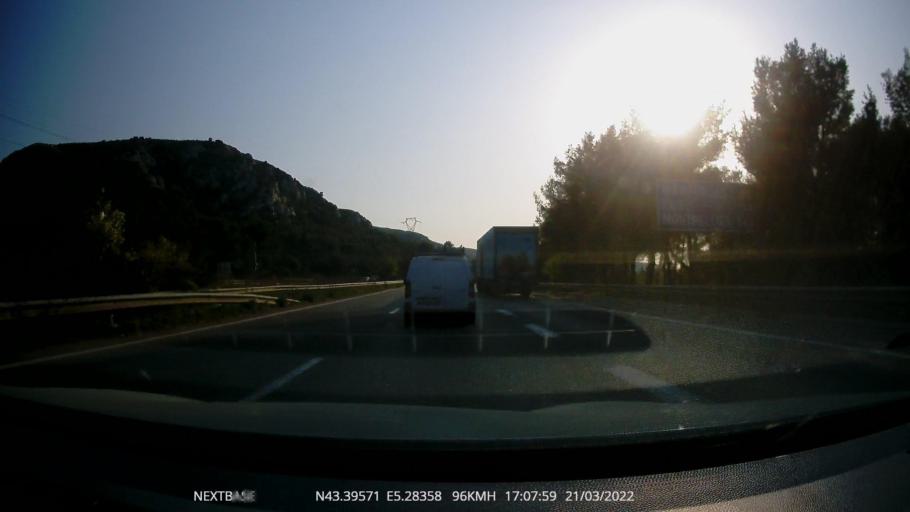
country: FR
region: Provence-Alpes-Cote d'Azur
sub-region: Departement des Bouches-du-Rhone
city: Les Pennes-Mirabeau
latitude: 43.3968
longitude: 5.2835
